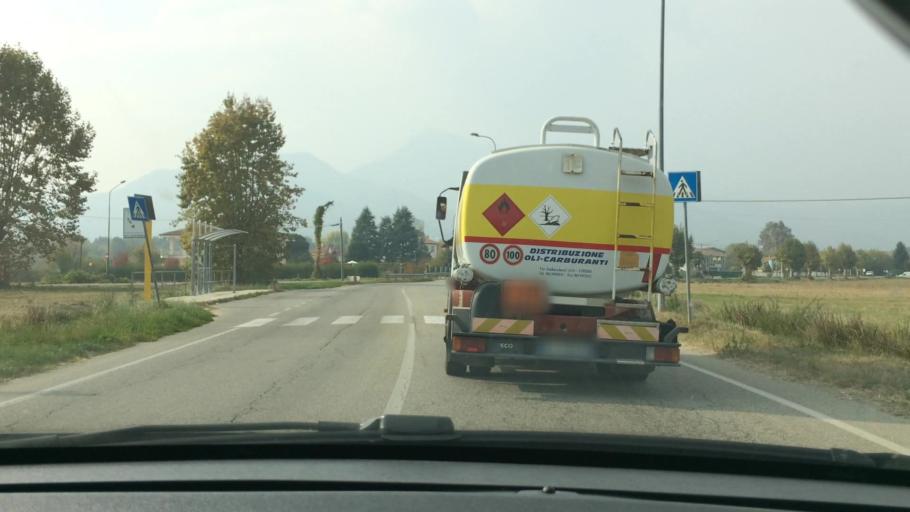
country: IT
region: Piedmont
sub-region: Provincia di Torino
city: Cumiana
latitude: 44.9577
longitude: 7.4074
